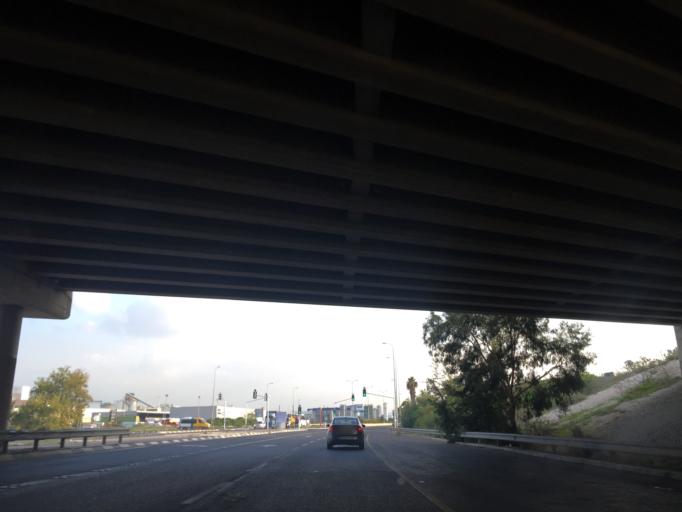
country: IL
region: Central District
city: Ramla
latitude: 31.9237
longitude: 34.8840
